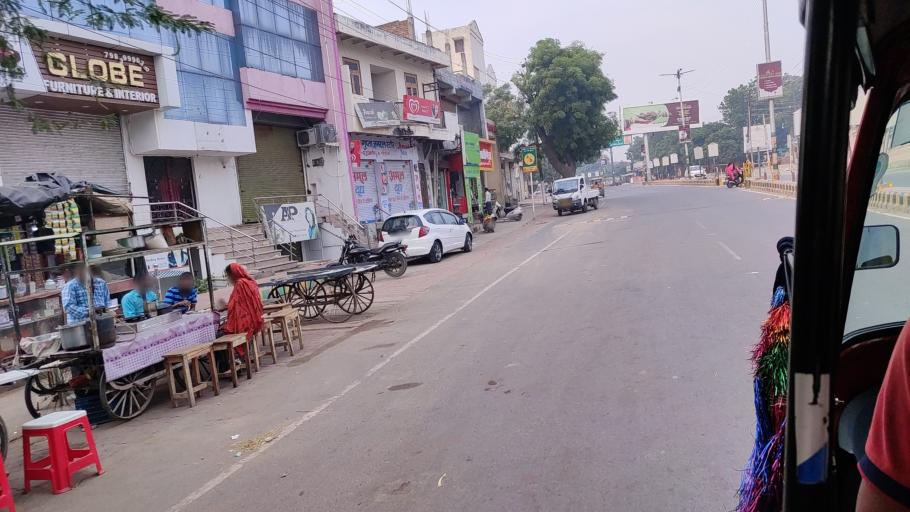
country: IN
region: Uttar Pradesh
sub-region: Mathura
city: Vrindavan
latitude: 27.5706
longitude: 77.6679
